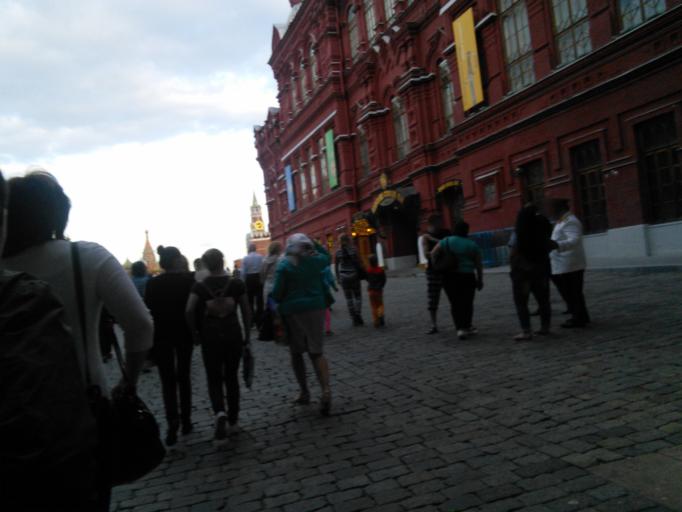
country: RU
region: Moscow
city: Moscow
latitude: 55.7557
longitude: 37.6179
